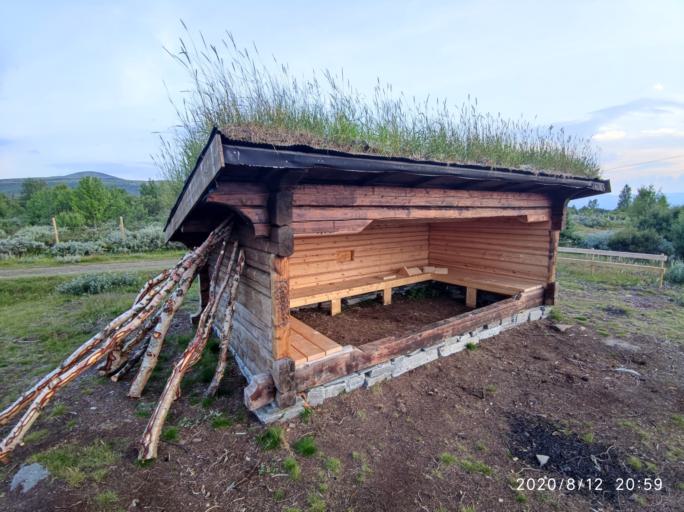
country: NO
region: Oppland
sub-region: Dovre
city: Dombas
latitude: 62.0929
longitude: 9.2178
